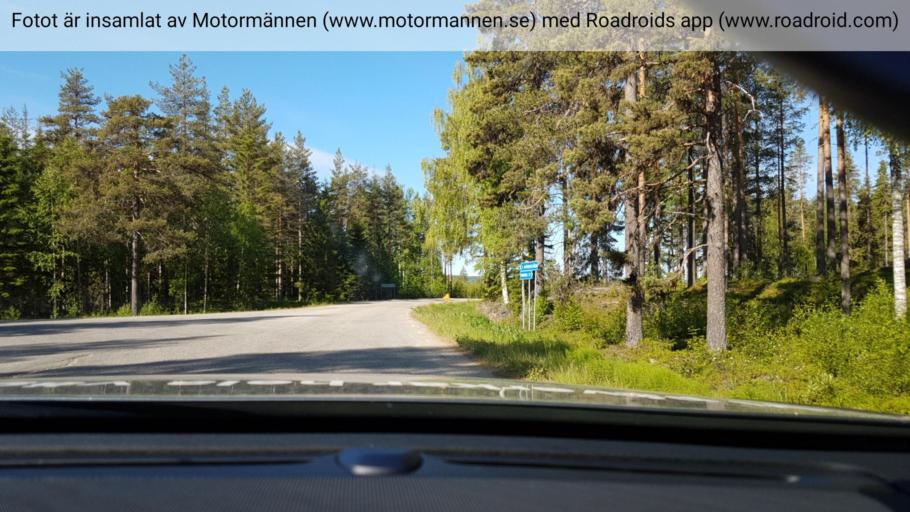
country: SE
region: Vaesterbotten
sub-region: Bjurholms Kommun
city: Bjurholm
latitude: 64.1301
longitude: 19.2992
